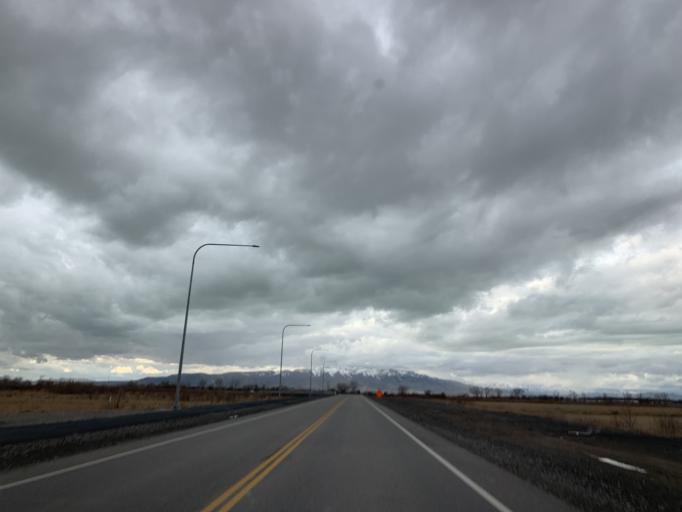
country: US
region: Utah
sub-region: Utah County
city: Provo
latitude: 40.2176
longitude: -111.6967
